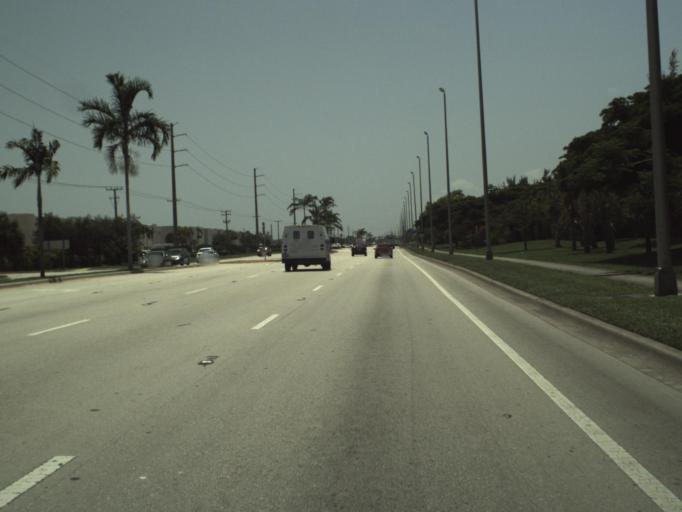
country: US
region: Florida
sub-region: Broward County
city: Tedder
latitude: 26.2961
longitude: -80.1526
